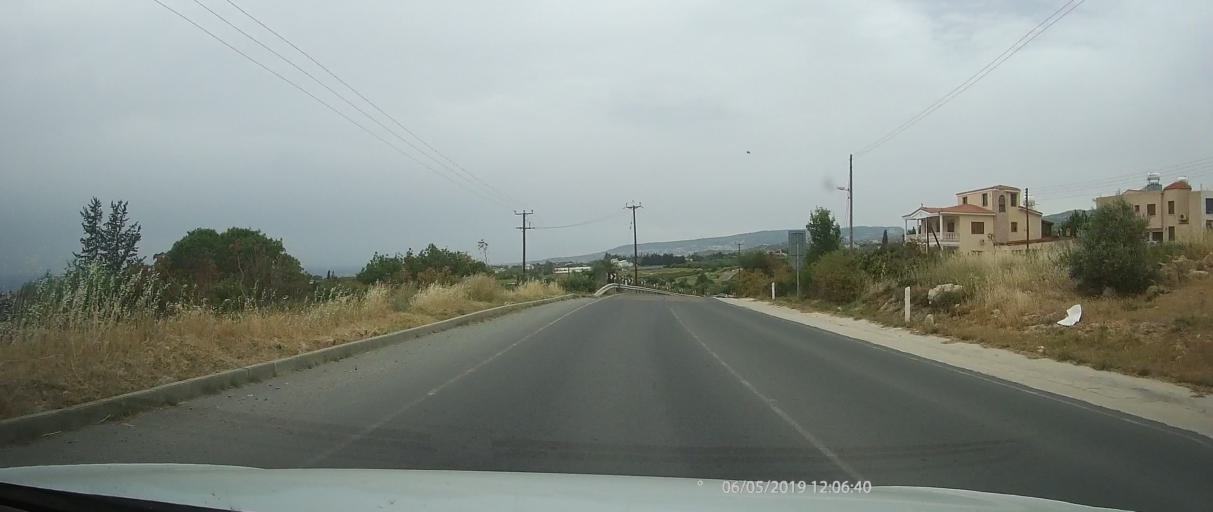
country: CY
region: Pafos
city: Empa
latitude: 34.8193
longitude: 32.4232
